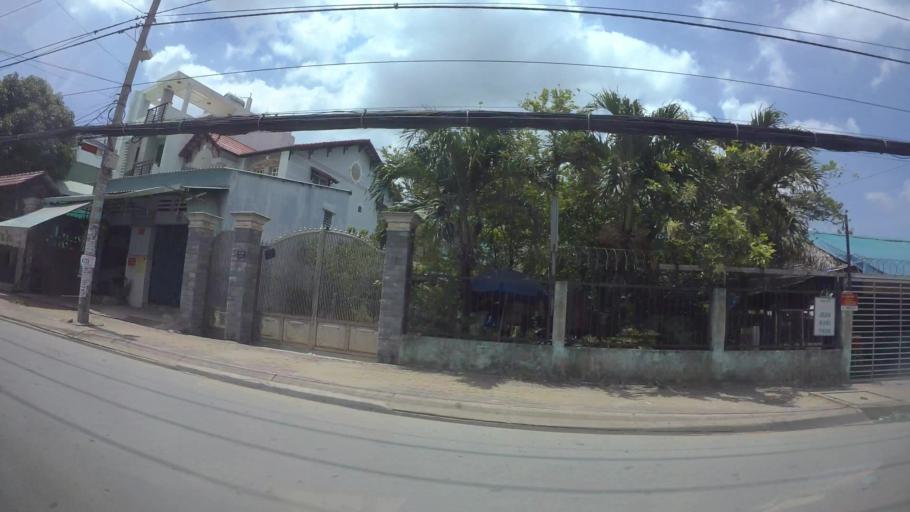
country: VN
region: Ho Chi Minh City
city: Quan Chin
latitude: 10.8369
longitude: 106.7816
